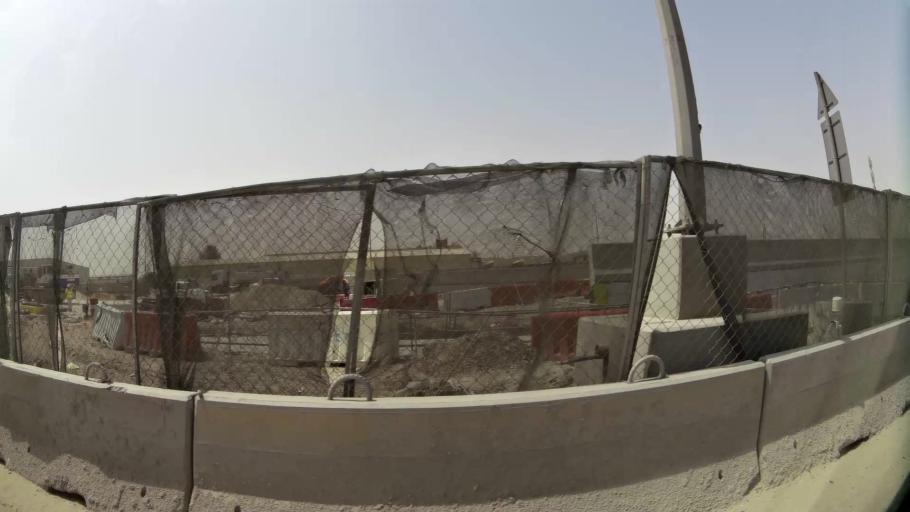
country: QA
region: Al Wakrah
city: Al Wukayr
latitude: 25.1903
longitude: 51.4573
